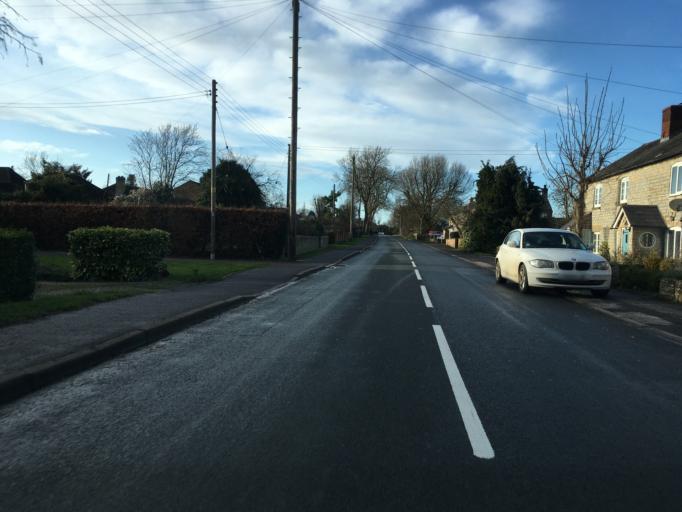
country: GB
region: England
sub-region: Warwickshire
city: Henley in Arden
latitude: 52.2227
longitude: -1.7690
